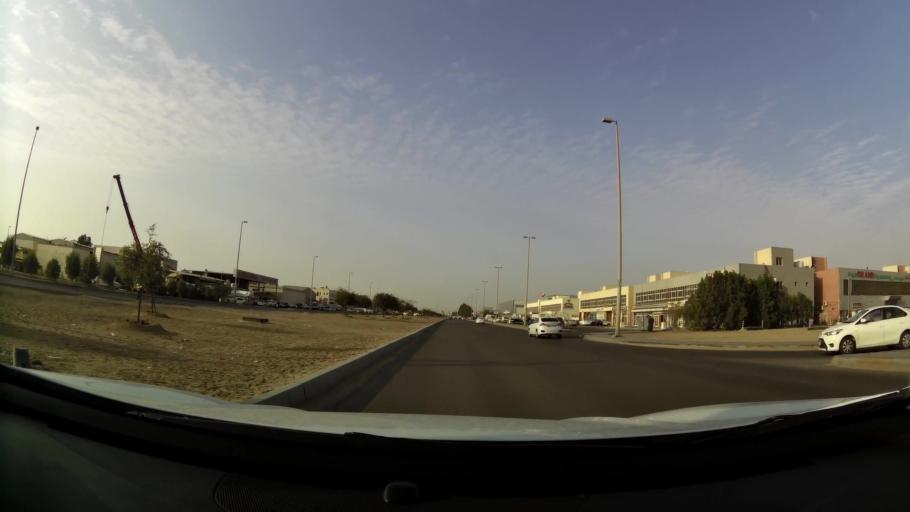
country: AE
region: Abu Dhabi
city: Abu Dhabi
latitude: 24.3646
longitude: 54.5165
